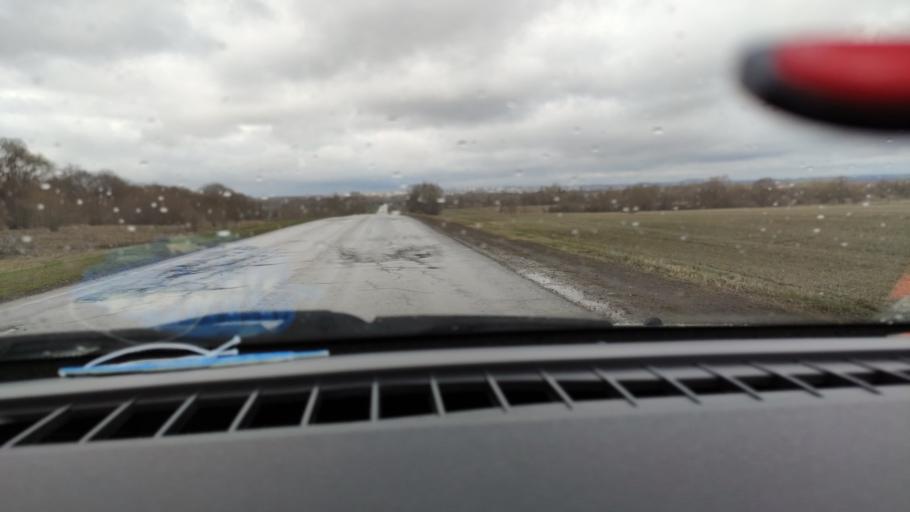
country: RU
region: Samara
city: Koshki
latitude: 54.1960
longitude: 50.5321
